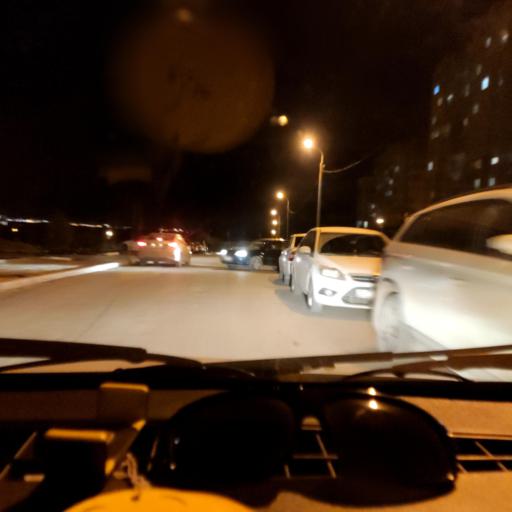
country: RU
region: Bashkortostan
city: Ufa
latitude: 54.6974
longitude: 55.9824
